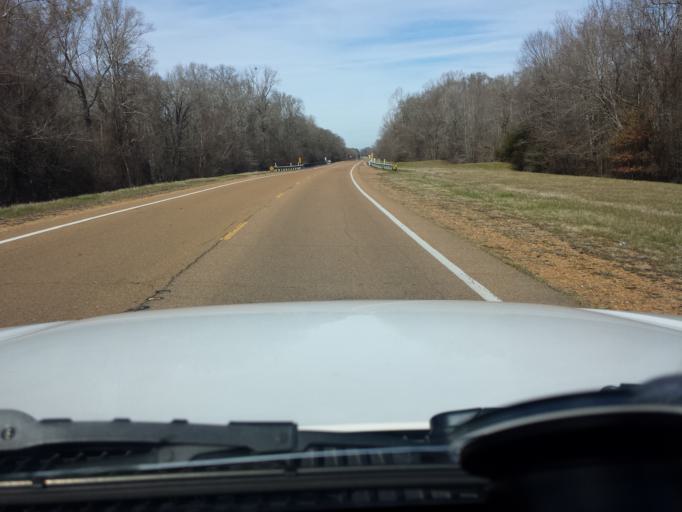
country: US
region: Mississippi
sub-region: Madison County
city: Canton
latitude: 32.7131
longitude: -90.0966
